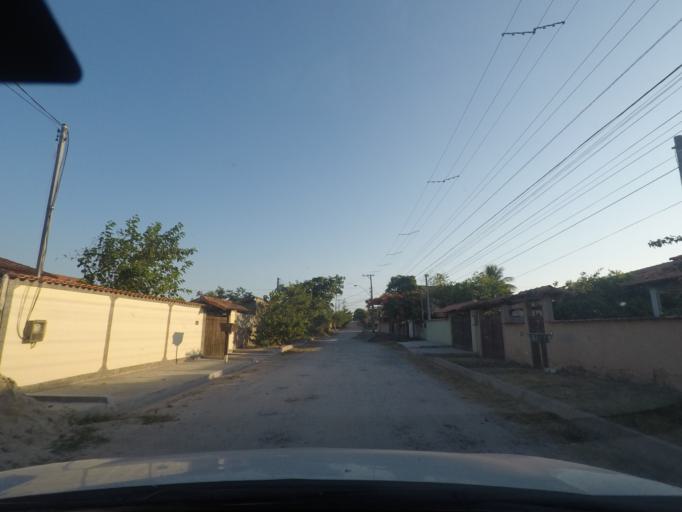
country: BR
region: Rio de Janeiro
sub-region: Marica
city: Marica
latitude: -22.9662
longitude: -42.9280
